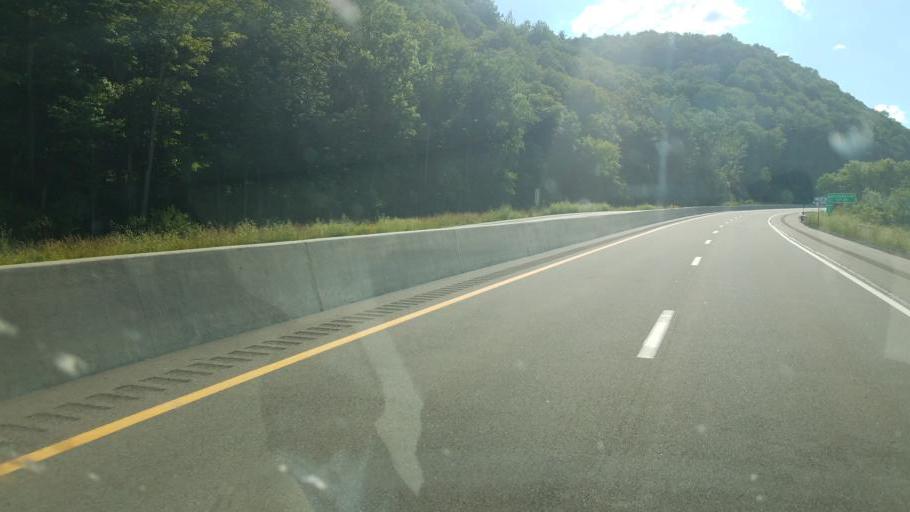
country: US
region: New York
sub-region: Cattaraugus County
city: Salamanca
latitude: 42.1478
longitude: -78.6829
